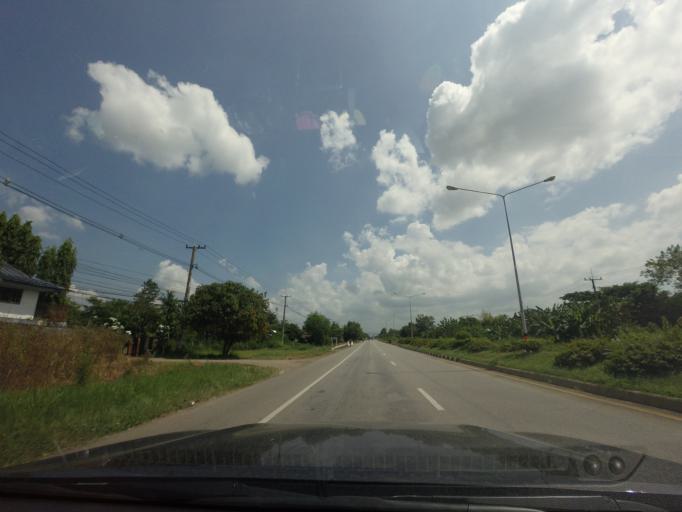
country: TH
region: Phetchabun
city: Phetchabun
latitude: 16.2576
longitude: 101.0579
